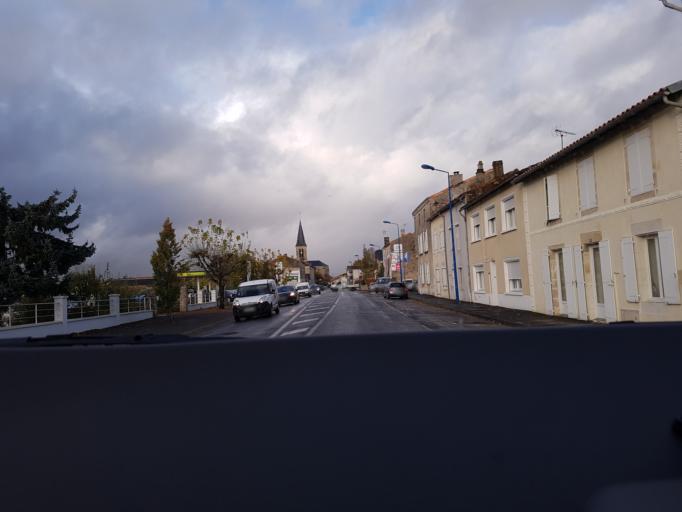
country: FR
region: Poitou-Charentes
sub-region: Departement des Deux-Sevres
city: Brioux-sur-Boutonne
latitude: 46.1386
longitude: -0.2210
